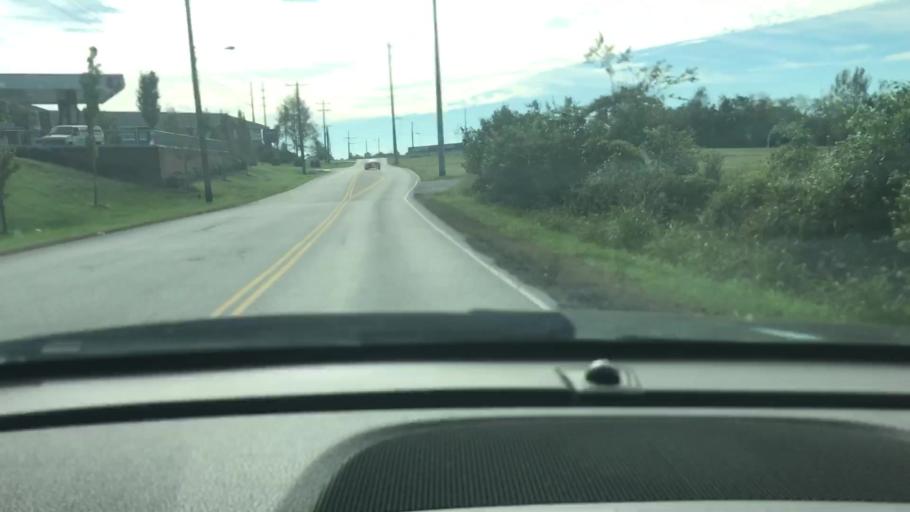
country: US
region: Tennessee
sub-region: Sumner County
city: Hendersonville
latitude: 36.3060
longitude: -86.6544
